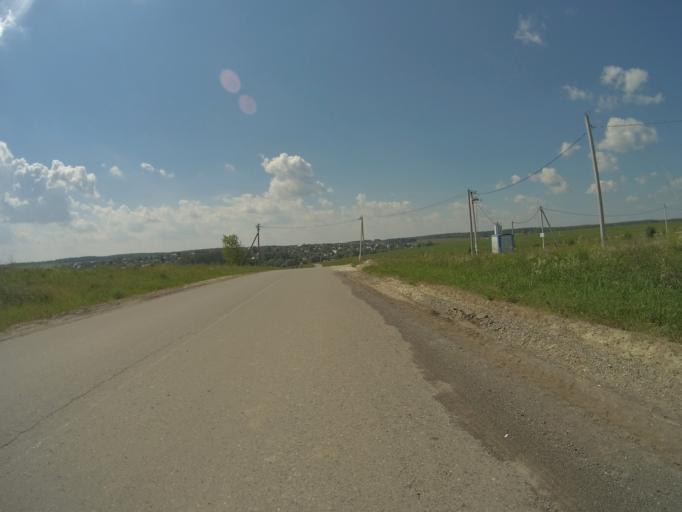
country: RU
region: Vladimir
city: Vladimir
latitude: 56.1517
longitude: 40.2652
